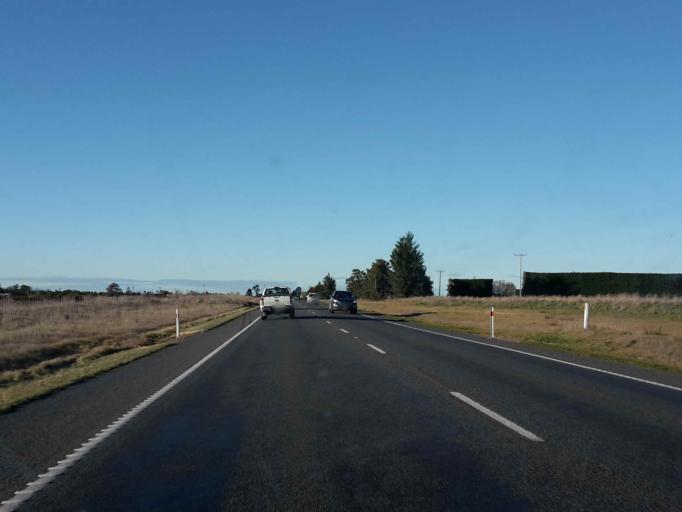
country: NZ
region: Canterbury
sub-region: Ashburton District
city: Tinwald
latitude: -44.0301
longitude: 171.4771
